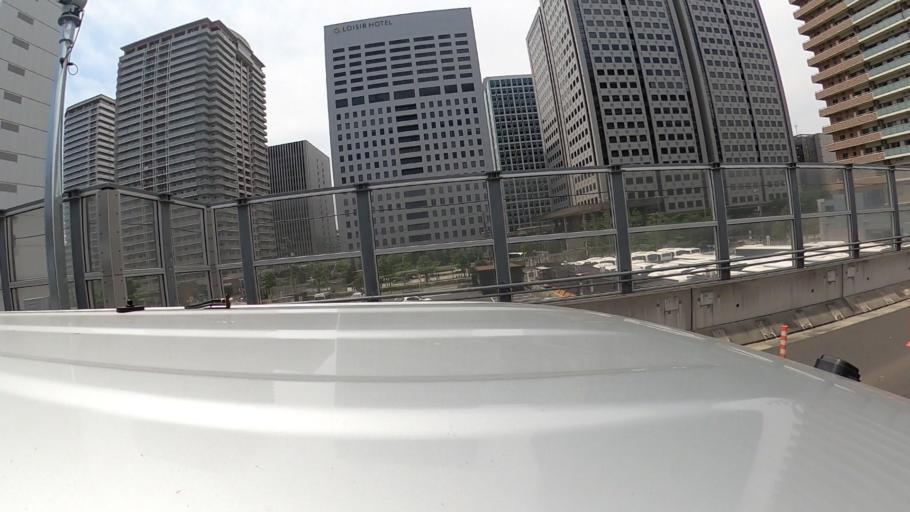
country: JP
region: Kanagawa
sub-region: Kawasaki-shi
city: Kawasaki
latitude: 35.6093
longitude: 139.7503
